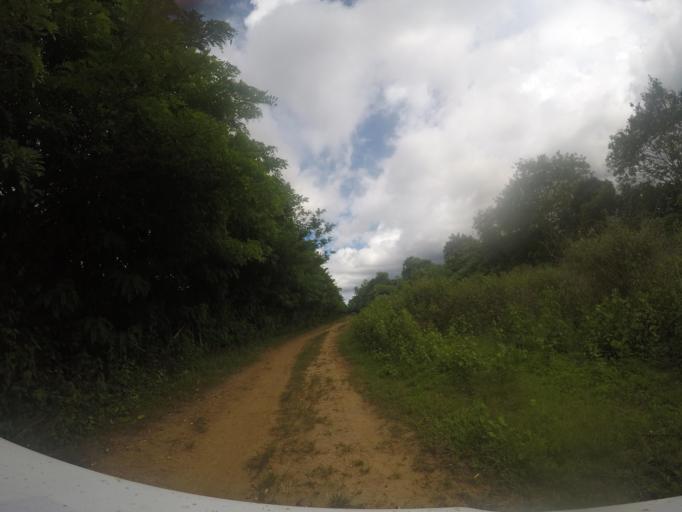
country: TL
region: Lautem
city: Lospalos
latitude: -8.5068
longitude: 127.0115
